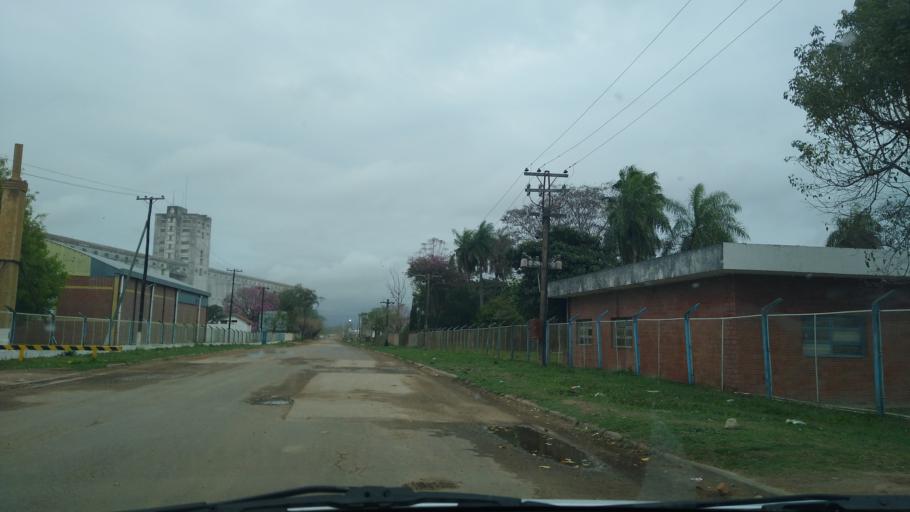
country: AR
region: Chaco
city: Barranqueras
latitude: -27.4702
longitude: -58.9078
